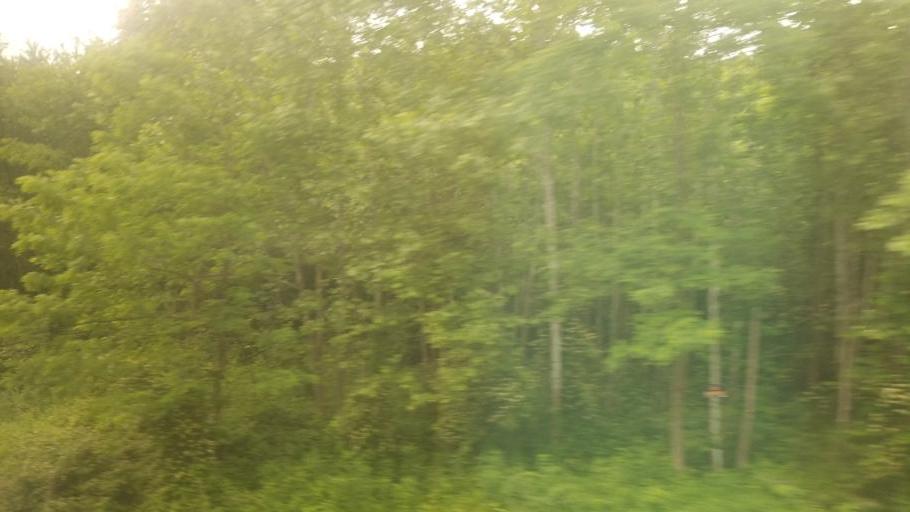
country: US
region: West Virginia
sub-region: Morgan County
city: Berkeley Springs
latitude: 39.5803
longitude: -78.3972
